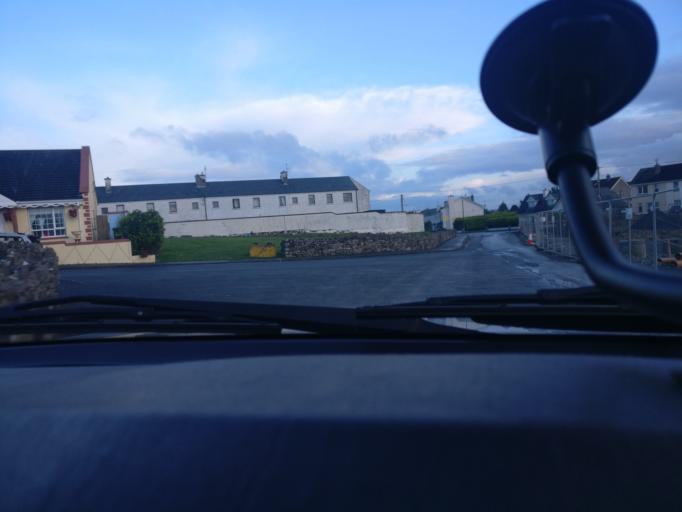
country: IE
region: Connaught
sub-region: County Galway
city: Loughrea
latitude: 53.1982
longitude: -8.5902
